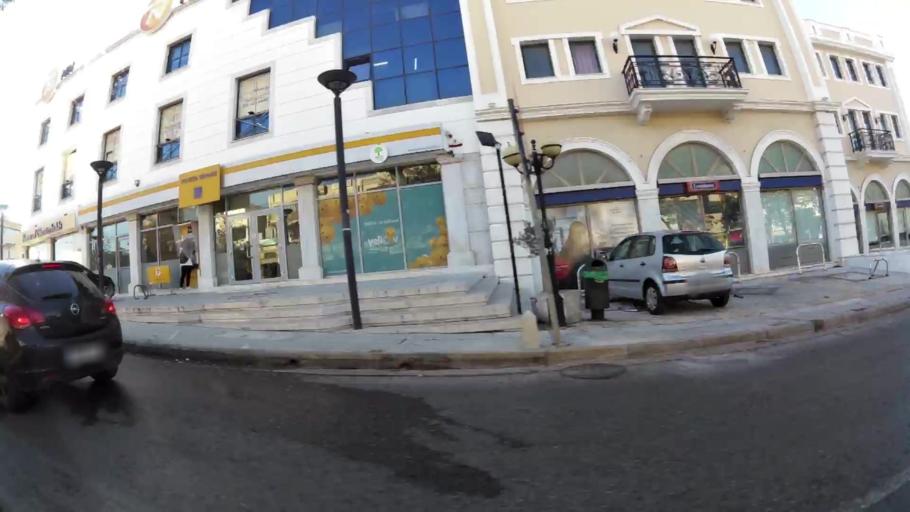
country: GR
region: Attica
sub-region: Nomarchia Athinas
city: Kifisia
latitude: 38.0718
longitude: 23.8111
